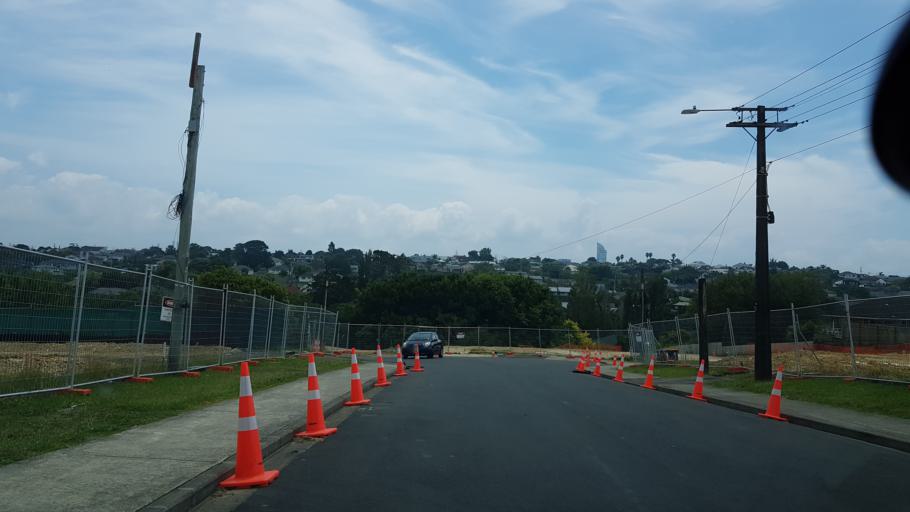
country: NZ
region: Auckland
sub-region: Auckland
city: North Shore
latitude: -36.8038
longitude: 174.7826
